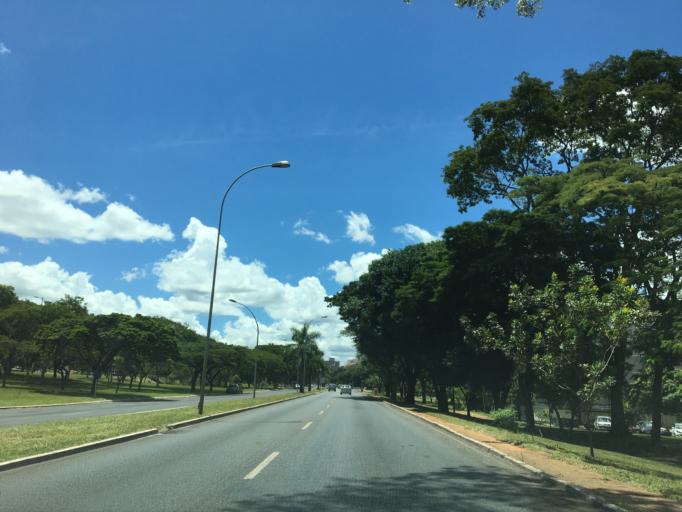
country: BR
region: Federal District
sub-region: Brasilia
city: Brasilia
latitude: -15.8149
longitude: -47.8969
